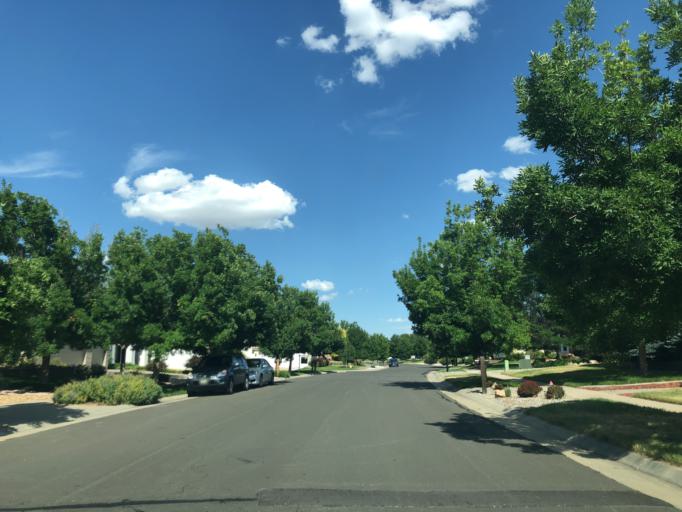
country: US
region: Colorado
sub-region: Arapahoe County
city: Dove Valley
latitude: 39.5960
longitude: -104.7844
